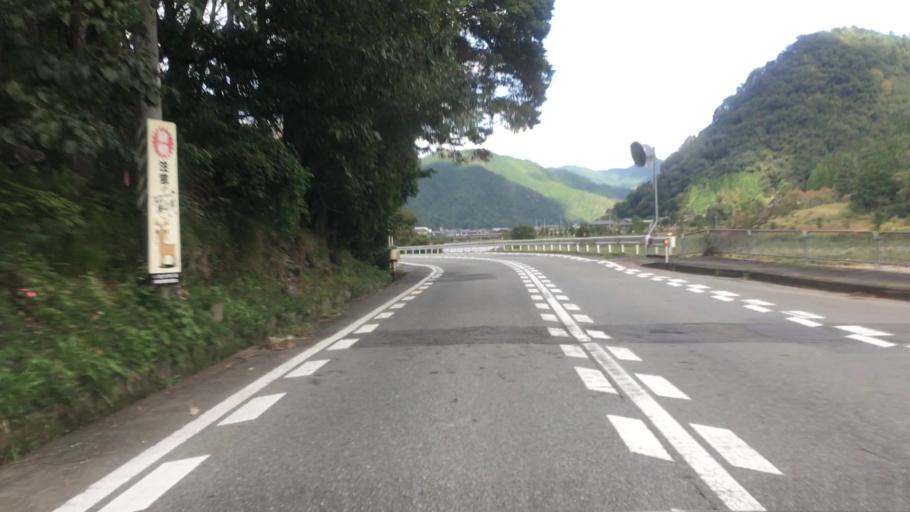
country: JP
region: Hyogo
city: Toyooka
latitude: 35.3661
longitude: 134.7606
